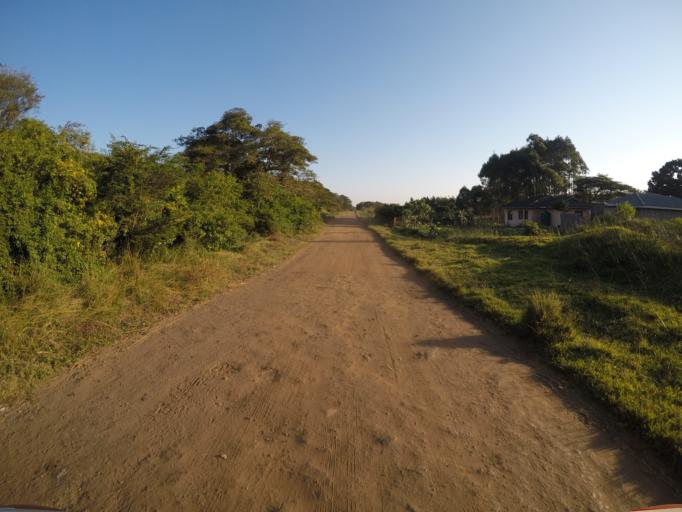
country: ZA
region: KwaZulu-Natal
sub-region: uThungulu District Municipality
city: KwaMbonambi
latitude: -28.6992
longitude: 32.1934
